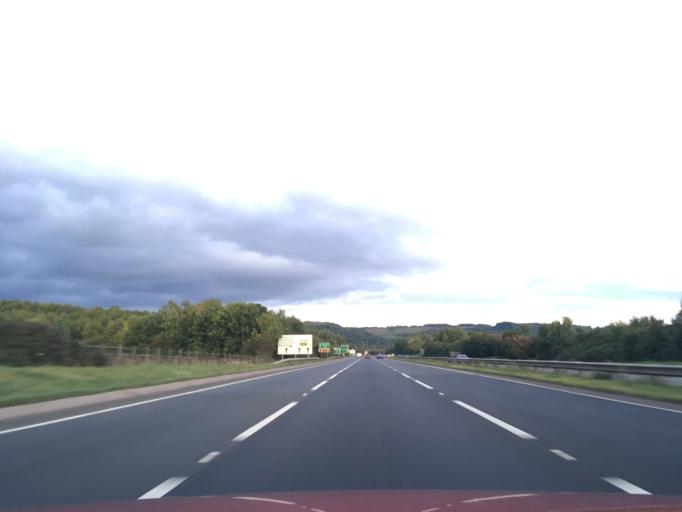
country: GB
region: England
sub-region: Gloucestershire
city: Churchdown
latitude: 51.8535
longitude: -2.1520
